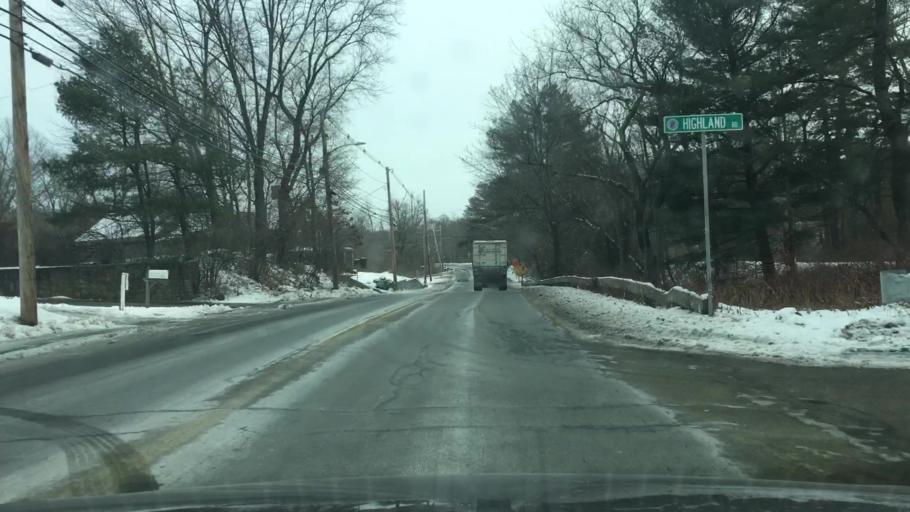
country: US
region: Massachusetts
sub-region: Essex County
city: Middleton
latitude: 42.5961
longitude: -70.9989
